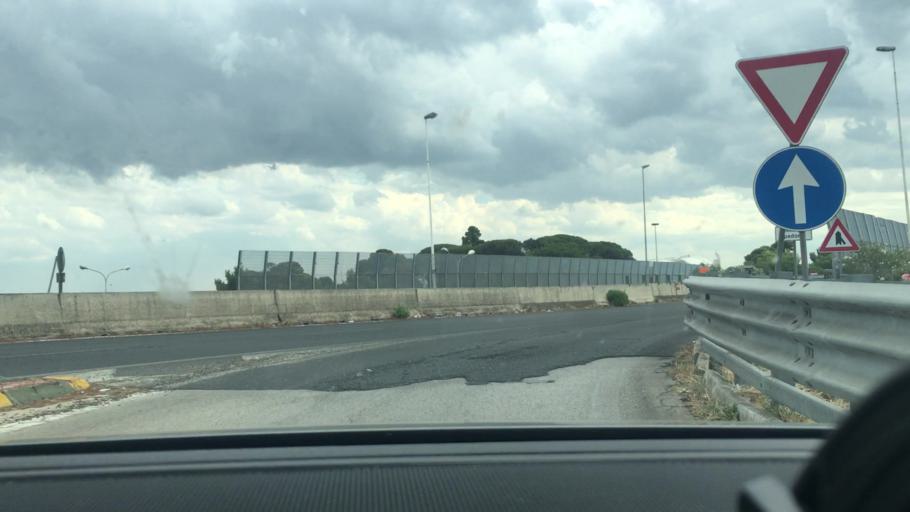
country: IT
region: Apulia
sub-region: Provincia di Bari
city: Bari
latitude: 41.0940
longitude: 16.8404
